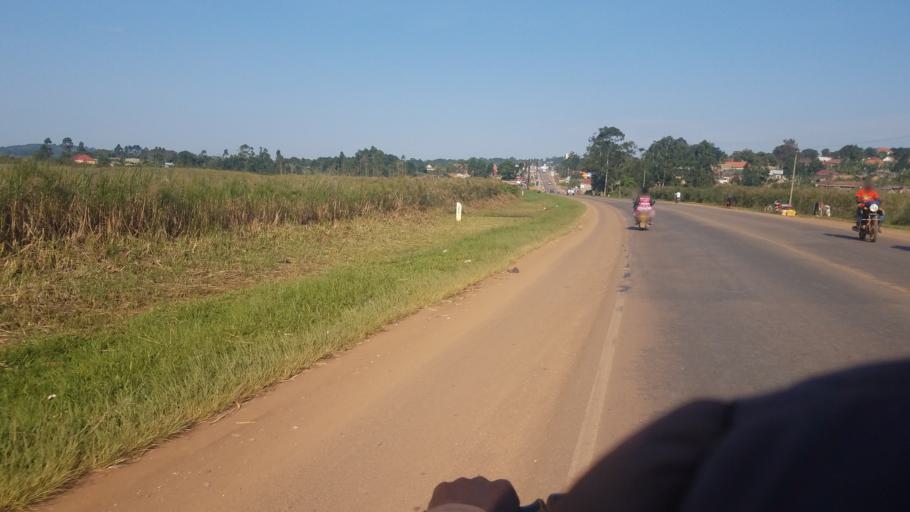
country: UG
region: Central Region
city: Masaka
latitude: -0.3366
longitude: 31.7132
